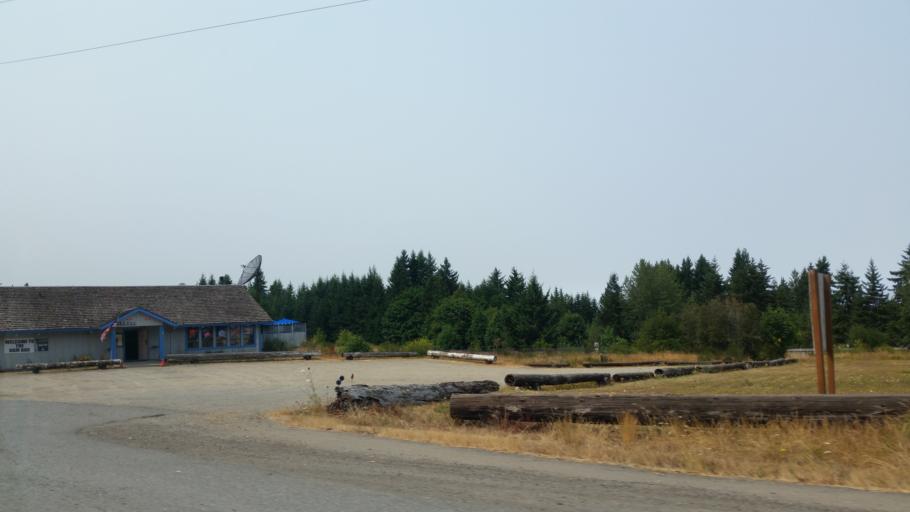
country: US
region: Washington
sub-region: Clallam County
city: Port Angeles
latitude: 48.0983
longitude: -123.5378
